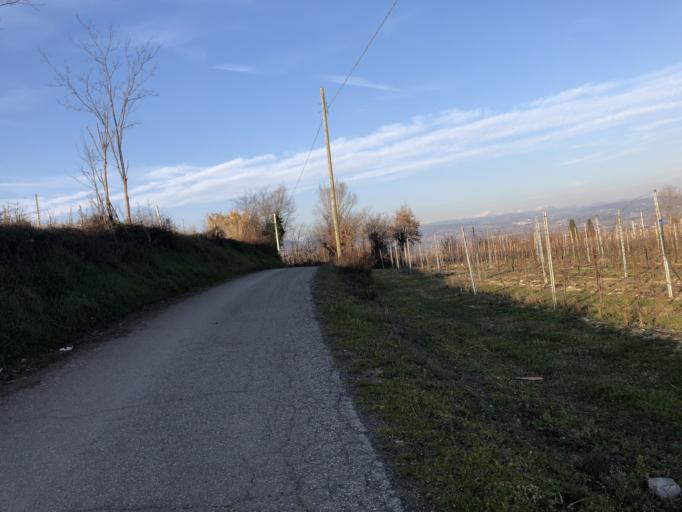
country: IT
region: Veneto
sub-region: Provincia di Verona
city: Pastrengo
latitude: 45.4738
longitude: 10.8174
